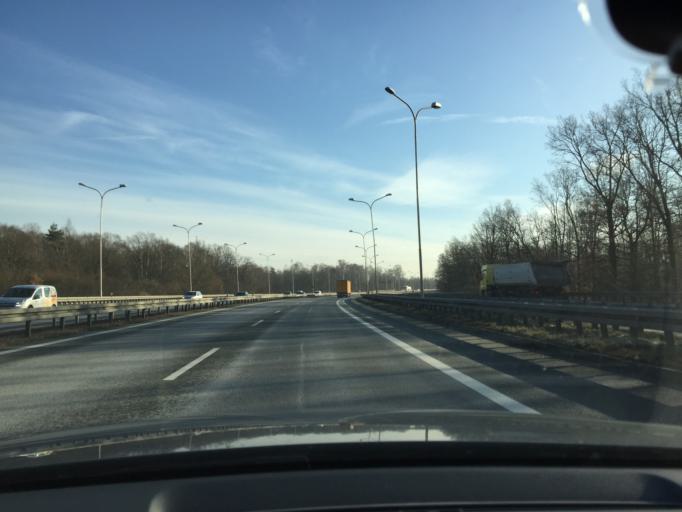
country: PL
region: Silesian Voivodeship
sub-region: Katowice
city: Katowice
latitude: 50.2401
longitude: 19.0564
